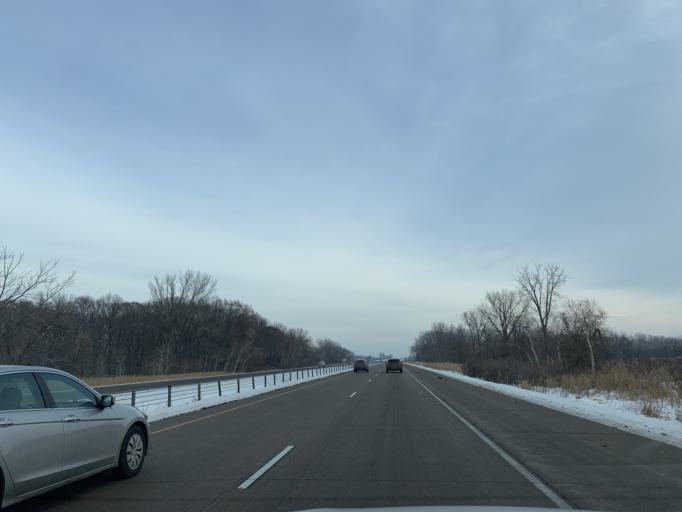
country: US
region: Minnesota
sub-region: Anoka County
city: Centerville
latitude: 45.2038
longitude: -93.0476
